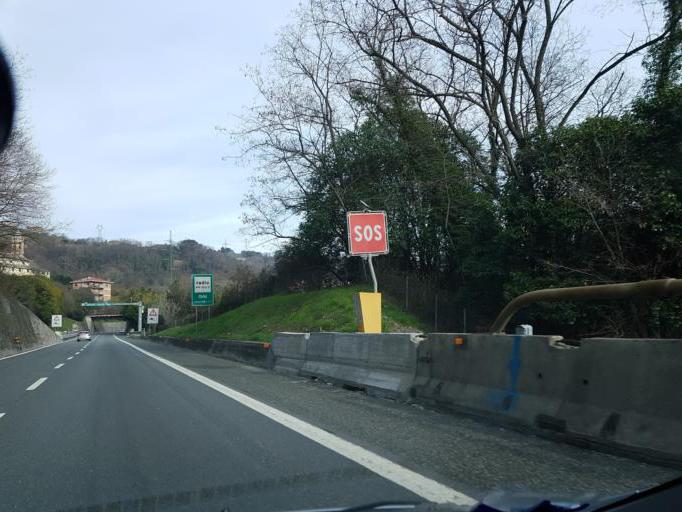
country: IT
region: Liguria
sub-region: Provincia di Genova
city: Manesseno
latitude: 44.4746
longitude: 8.9107
